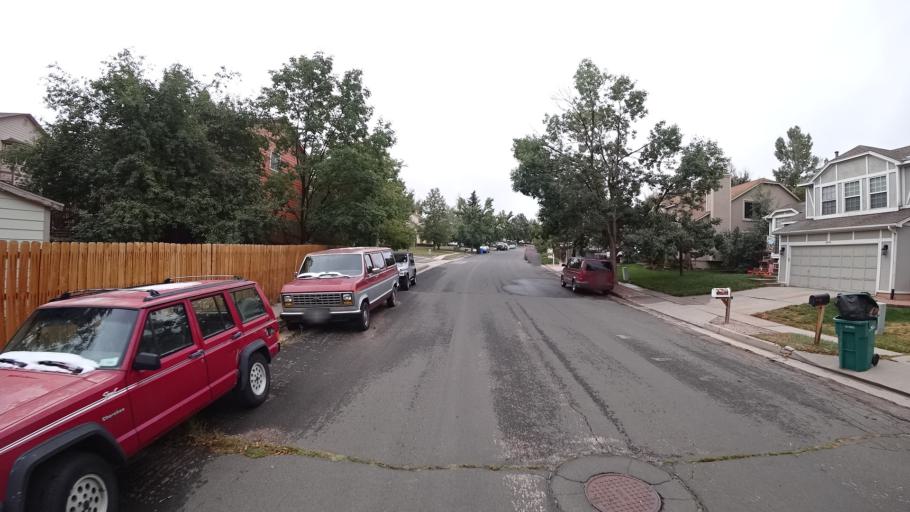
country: US
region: Colorado
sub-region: El Paso County
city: Cimarron Hills
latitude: 38.9264
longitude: -104.7607
